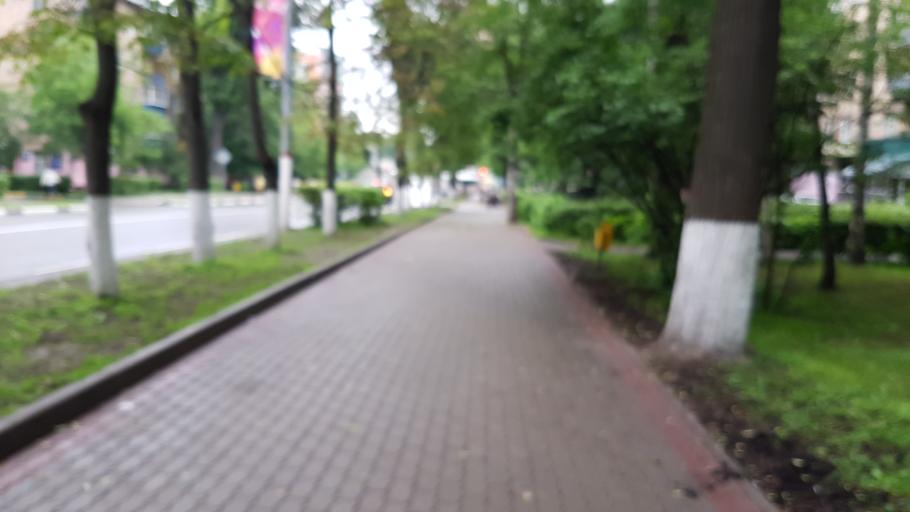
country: RU
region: Moscow
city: Khimki
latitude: 55.8926
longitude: 37.4487
